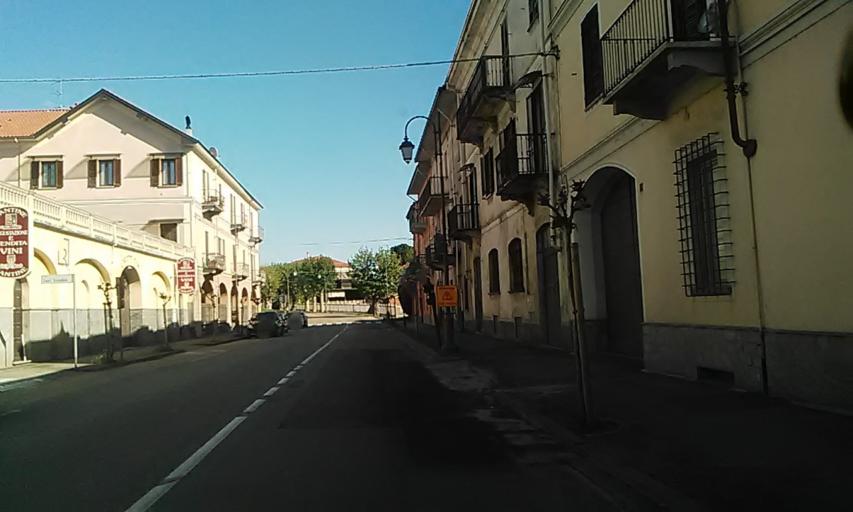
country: IT
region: Piedmont
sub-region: Provincia di Novara
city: Romagnano Sesia
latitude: 45.6313
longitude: 8.3829
